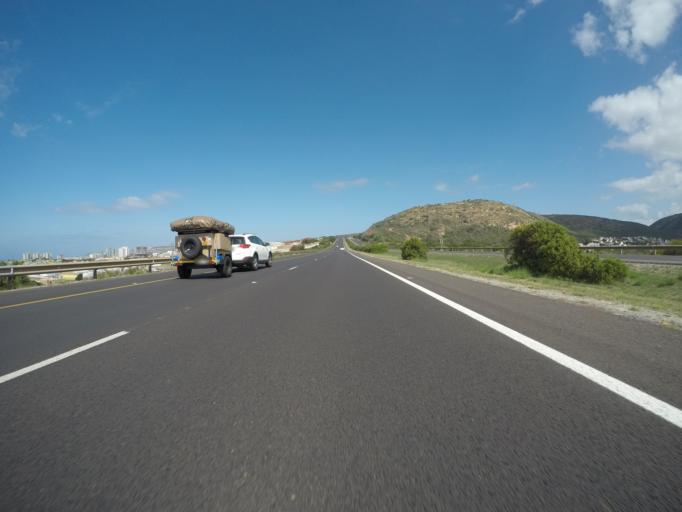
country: ZA
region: Western Cape
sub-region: Eden District Municipality
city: Mossel Bay
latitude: -34.1504
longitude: 22.0989
